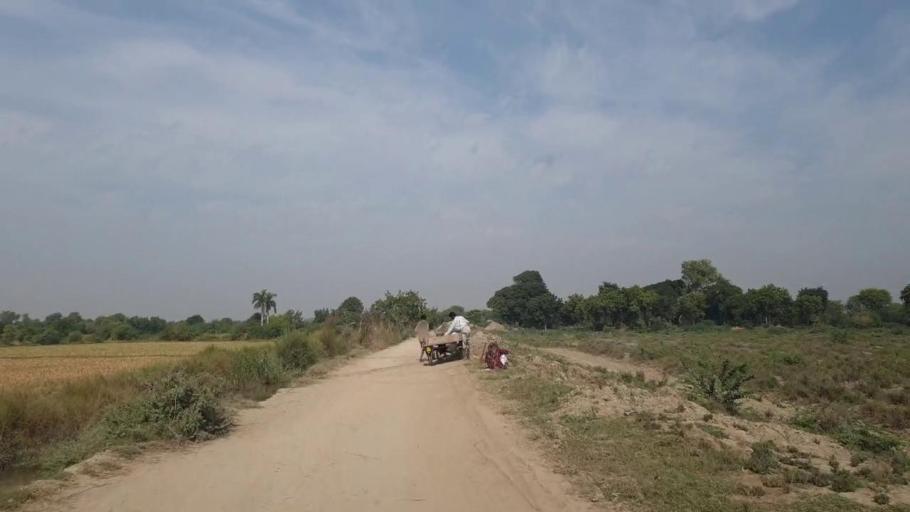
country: PK
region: Sindh
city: Tando Bago
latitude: 24.8918
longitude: 69.0007
